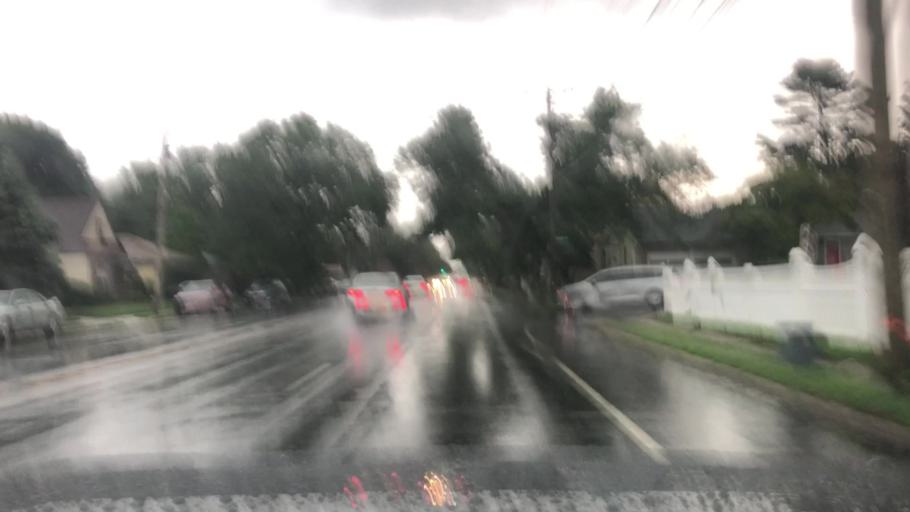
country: US
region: New York
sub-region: Nassau County
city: South Hempstead
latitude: 40.6912
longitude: -73.6138
